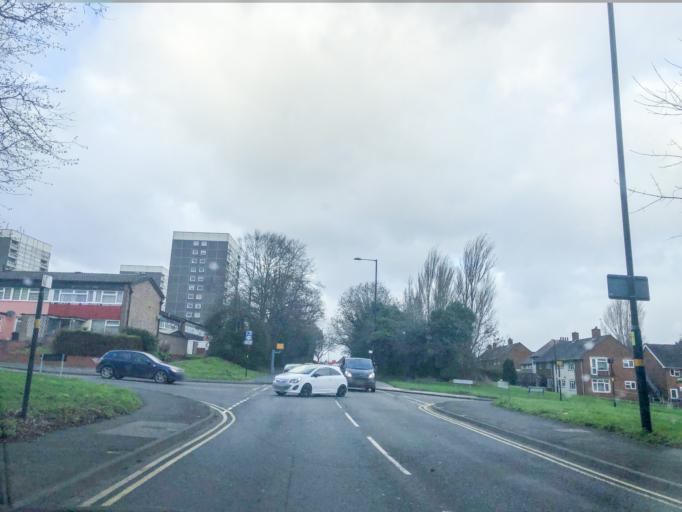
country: GB
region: England
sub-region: Solihull
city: Tidbury Green
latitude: 52.4079
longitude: -1.8881
